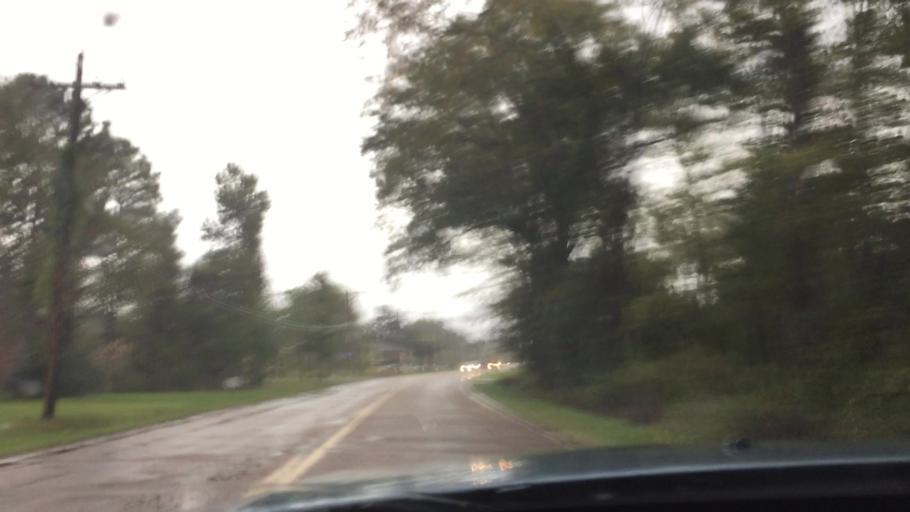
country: US
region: Louisiana
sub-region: East Baton Rouge Parish
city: Monticello
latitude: 30.4489
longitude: -91.0296
